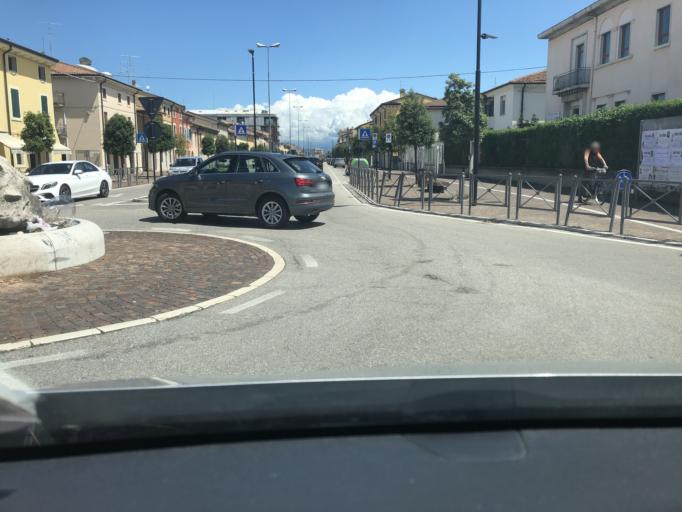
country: IT
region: Veneto
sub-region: Provincia di Verona
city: Villafranca di Verona
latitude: 45.3513
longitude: 10.8398
